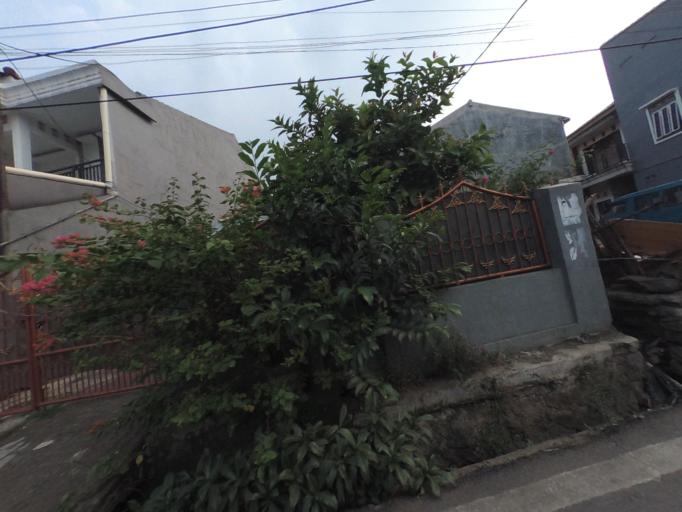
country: ID
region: West Java
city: Ciampea
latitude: -6.5745
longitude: 106.6638
